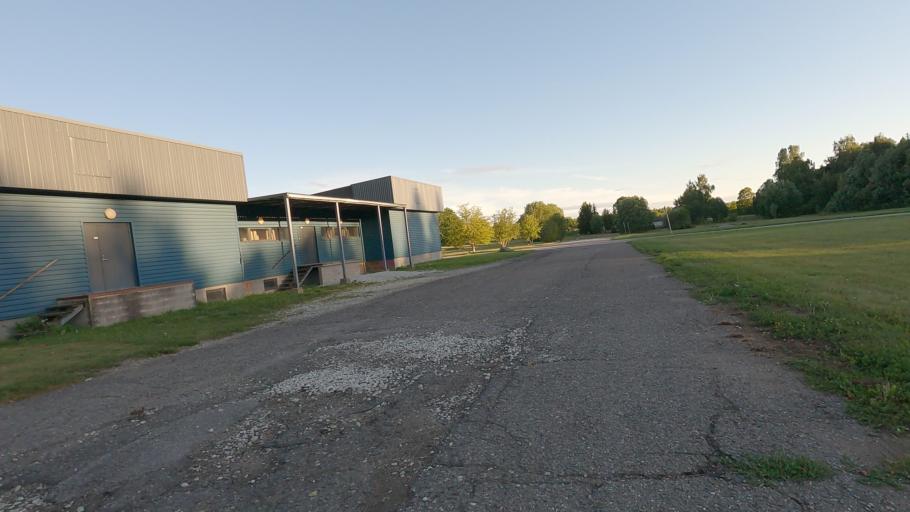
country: EE
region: Raplamaa
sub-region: Rapla vald
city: Rapla
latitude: 58.9995
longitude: 24.7809
